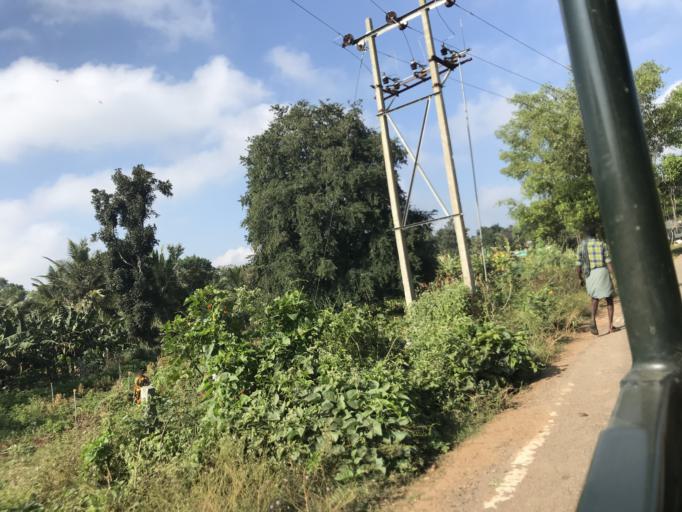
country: IN
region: Karnataka
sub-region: Mysore
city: Heggadadevankote
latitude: 11.9468
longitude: 76.2589
